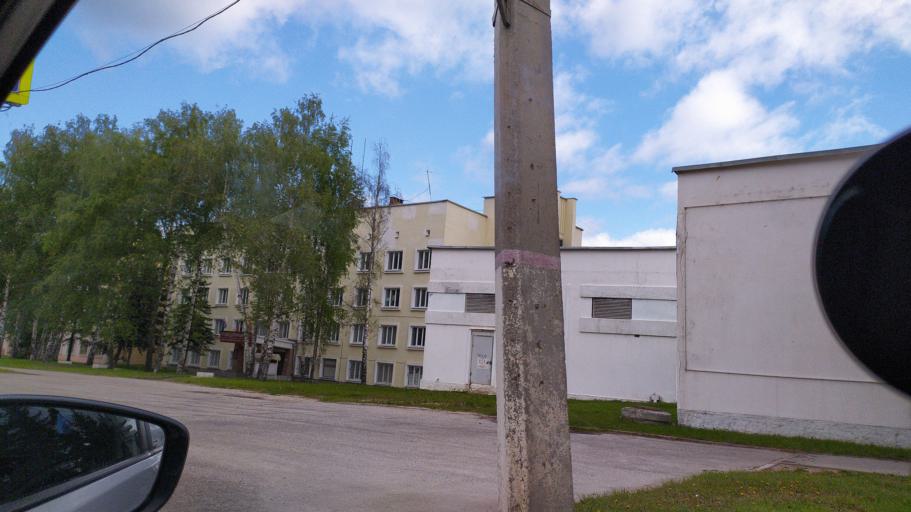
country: RU
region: Chuvashia
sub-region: Cheboksarskiy Rayon
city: Cheboksary
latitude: 56.1321
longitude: 47.2845
